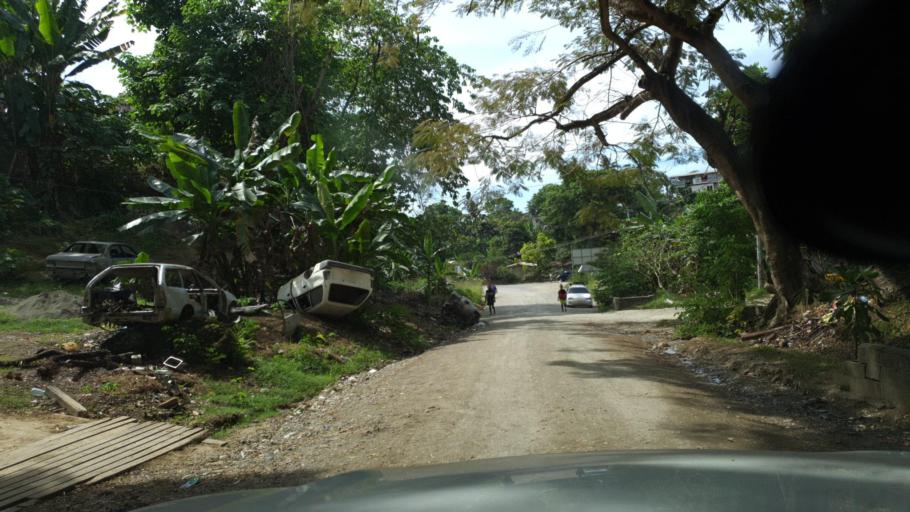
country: SB
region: Guadalcanal
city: Honiara
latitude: -9.4358
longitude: 159.9855
